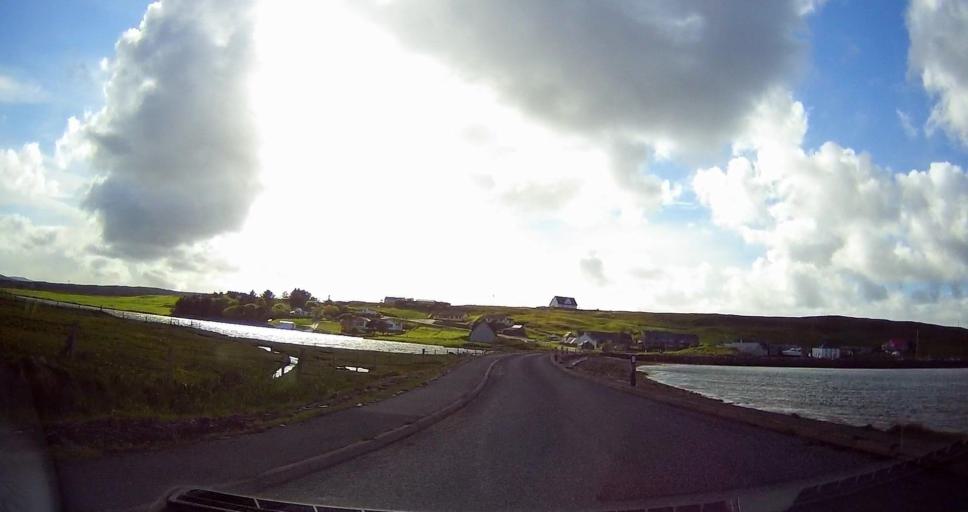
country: GB
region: Scotland
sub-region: Shetland Islands
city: Shetland
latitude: 60.3692
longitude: -1.1289
